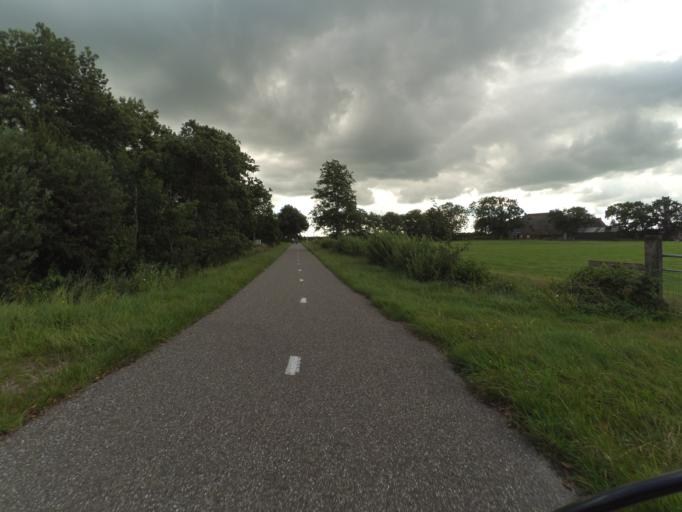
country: NL
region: Friesland
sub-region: Gemeente Tytsjerksteradiel
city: Hurdegaryp
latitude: 53.2063
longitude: 5.9589
